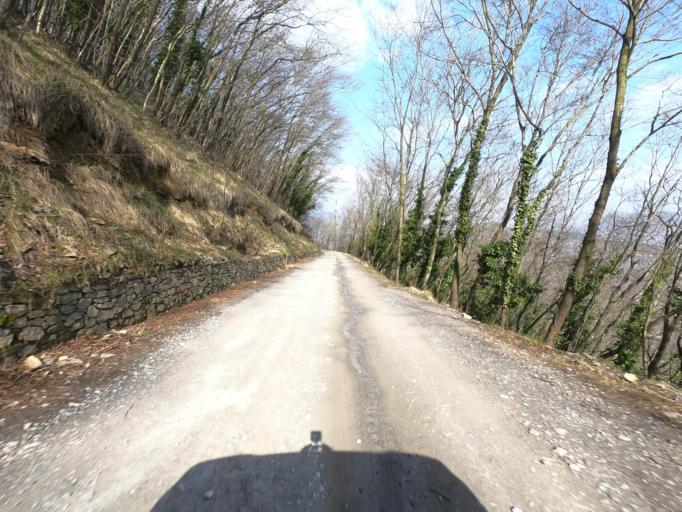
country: IT
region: Liguria
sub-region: Provincia di Savona
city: Balestrino
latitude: 44.1115
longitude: 8.1604
